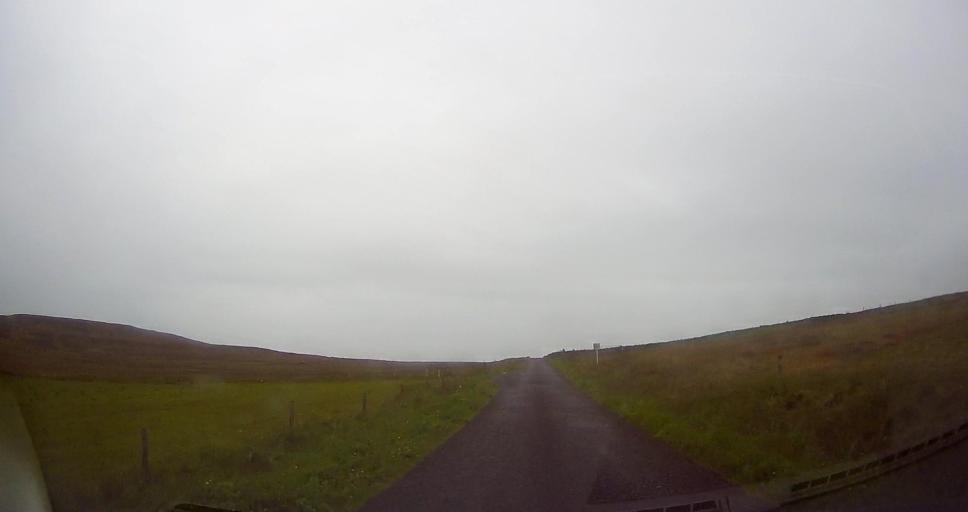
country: GB
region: Scotland
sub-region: Orkney Islands
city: Orkney
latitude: 59.1070
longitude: -3.1252
